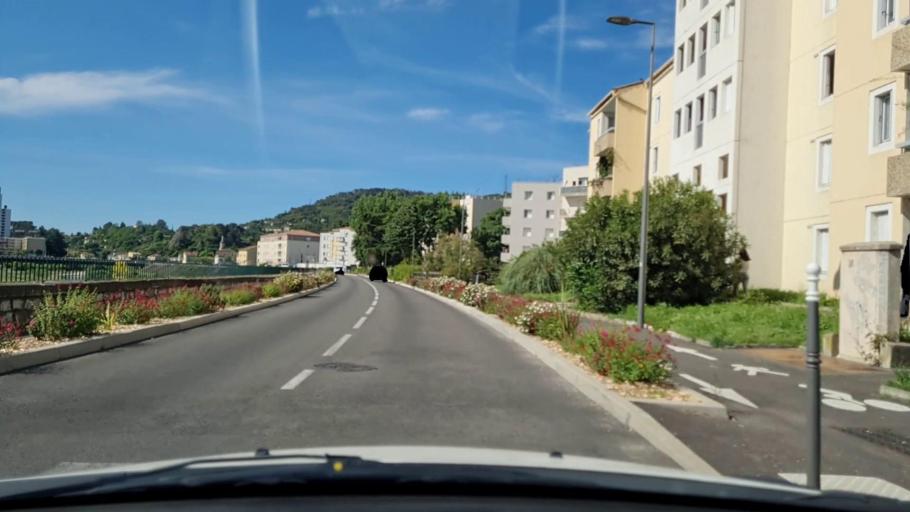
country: FR
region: Languedoc-Roussillon
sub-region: Departement du Gard
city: Ales
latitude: 44.1305
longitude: 4.0723
